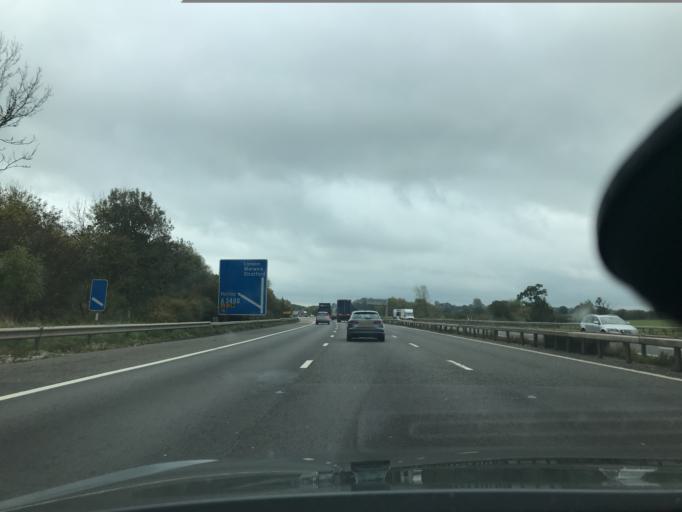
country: GB
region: England
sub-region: Warwickshire
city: Henley in Arden
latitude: 52.3381
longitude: -1.7833
